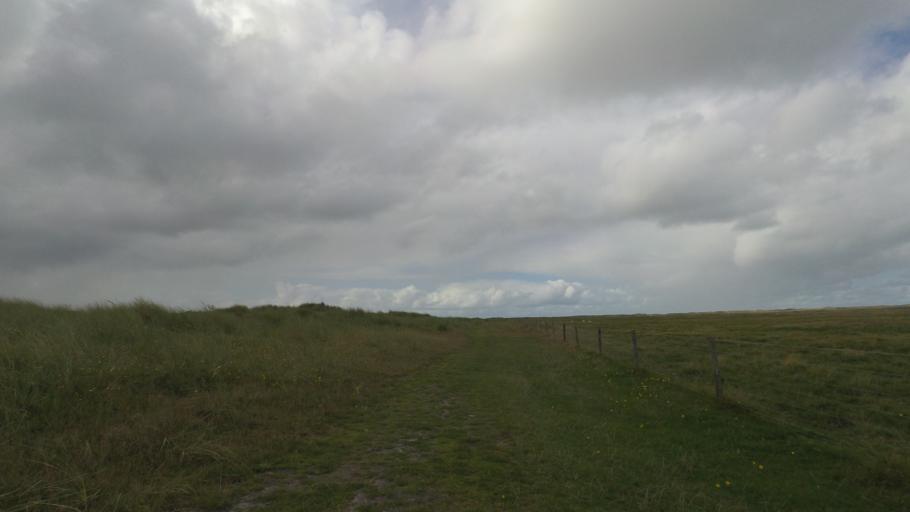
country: NL
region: Friesland
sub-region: Gemeente Ameland
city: Nes
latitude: 53.4512
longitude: 5.8535
